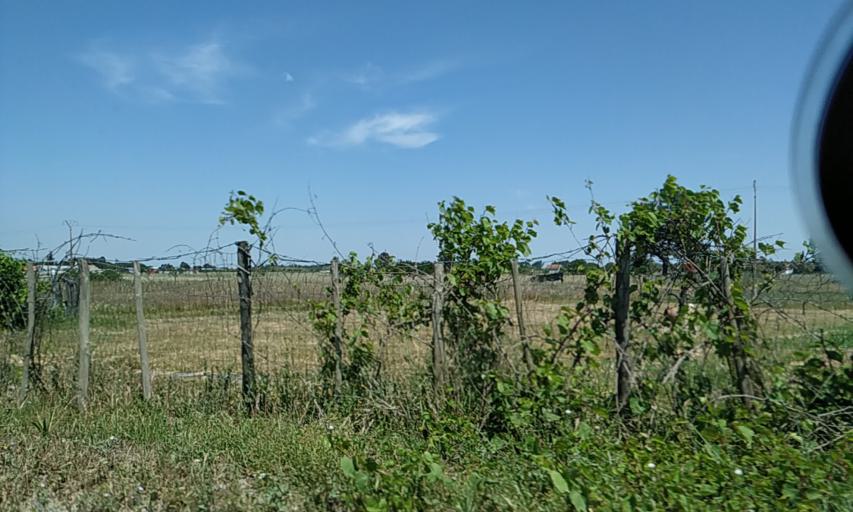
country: PT
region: Setubal
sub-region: Palmela
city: Pinhal Novo
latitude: 38.6427
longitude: -8.7432
